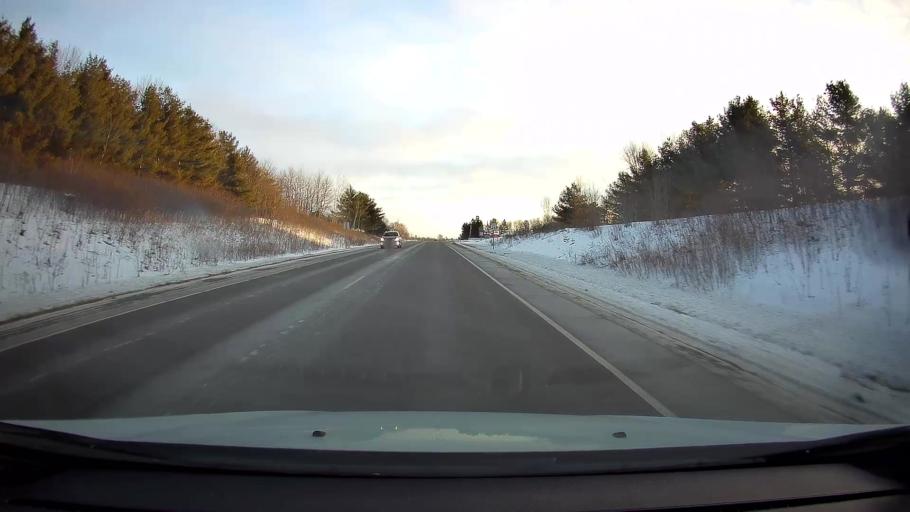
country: US
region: Wisconsin
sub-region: Polk County
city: Clear Lake
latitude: 45.2553
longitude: -92.2731
